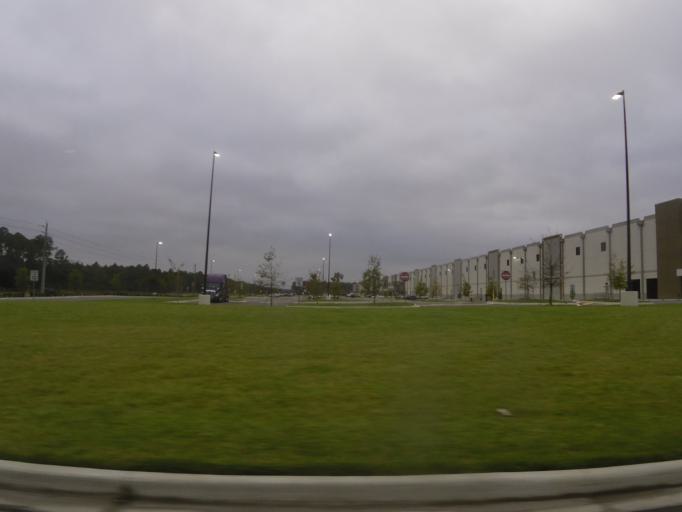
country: US
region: Florida
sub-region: Duval County
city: Baldwin
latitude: 30.2472
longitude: -81.8606
